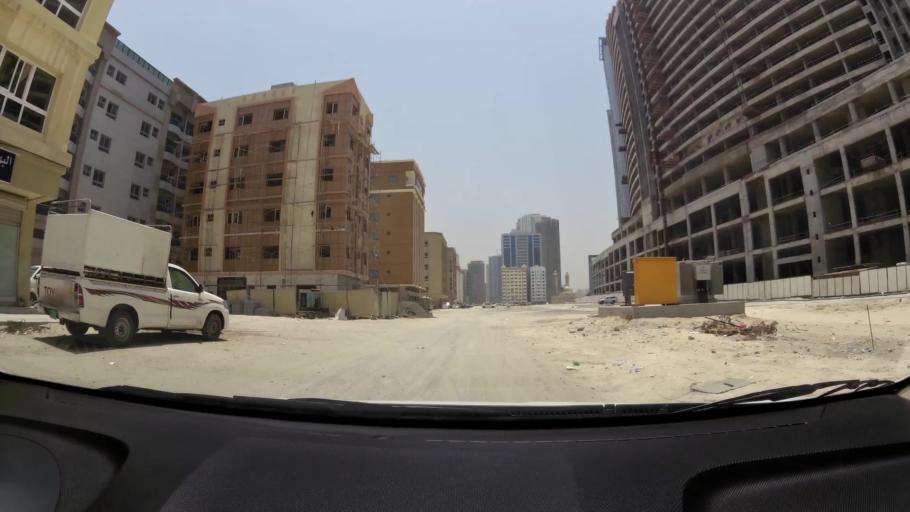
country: AE
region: Ash Shariqah
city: Sharjah
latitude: 25.3319
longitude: 55.3635
